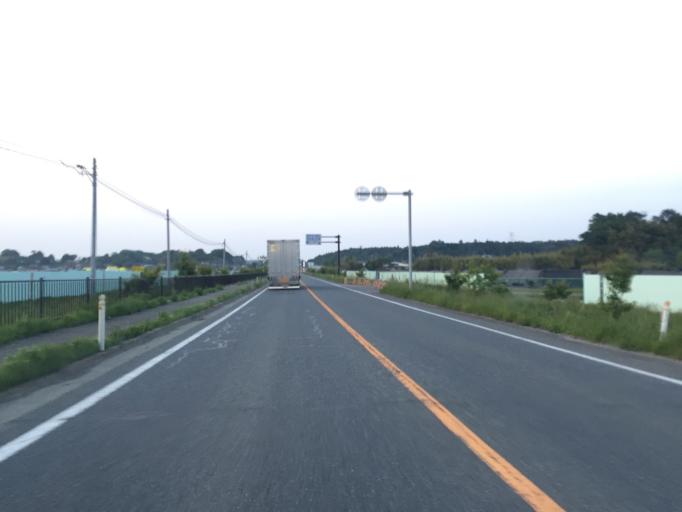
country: JP
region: Fukushima
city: Namie
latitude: 37.5993
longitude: 141.0038
